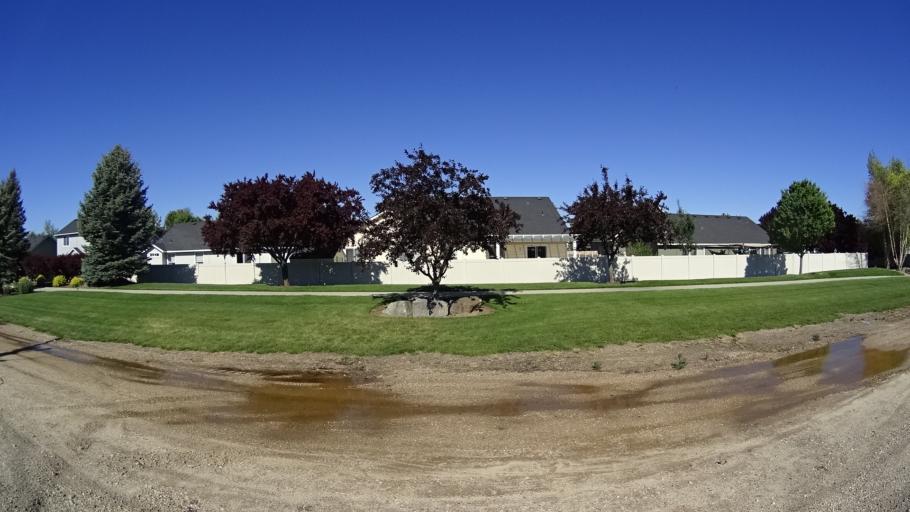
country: US
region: Idaho
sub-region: Ada County
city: Meridian
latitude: 43.6356
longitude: -116.4536
